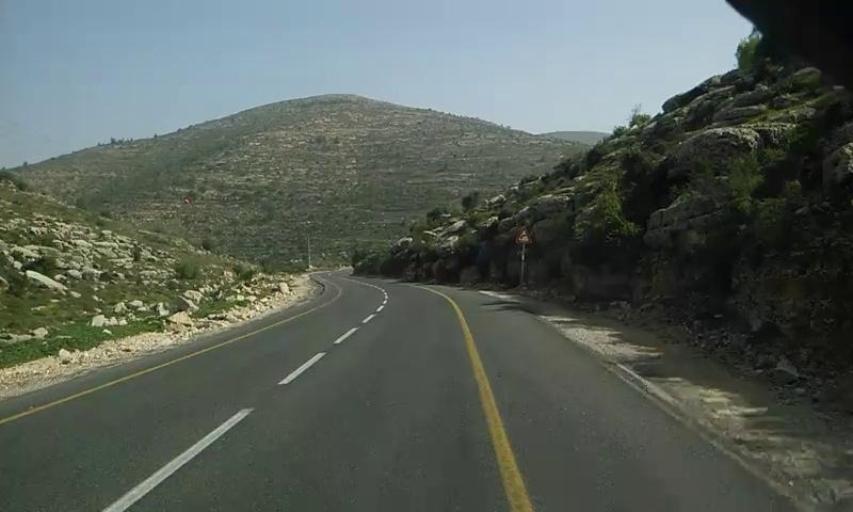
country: PS
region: West Bank
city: `Atarah
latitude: 32.0006
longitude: 35.2274
